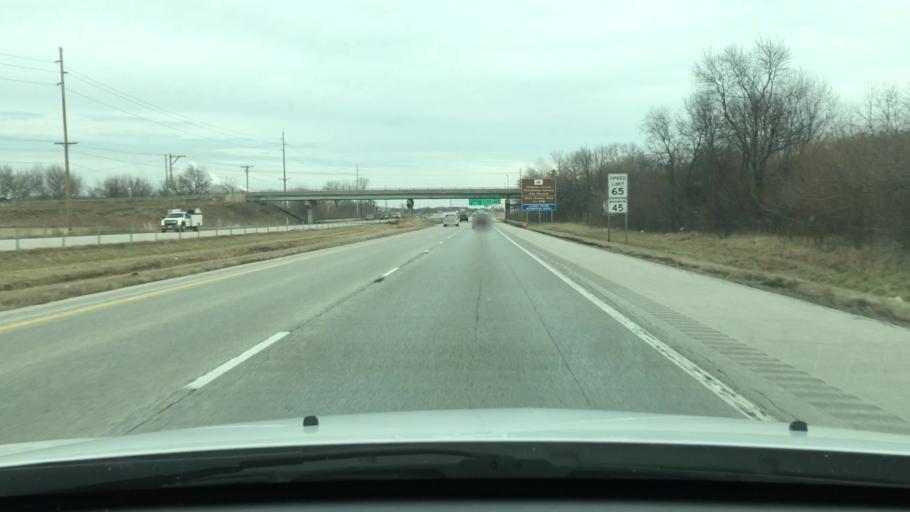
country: US
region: Illinois
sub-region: Sangamon County
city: Southern View
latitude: 39.7425
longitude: -89.6557
